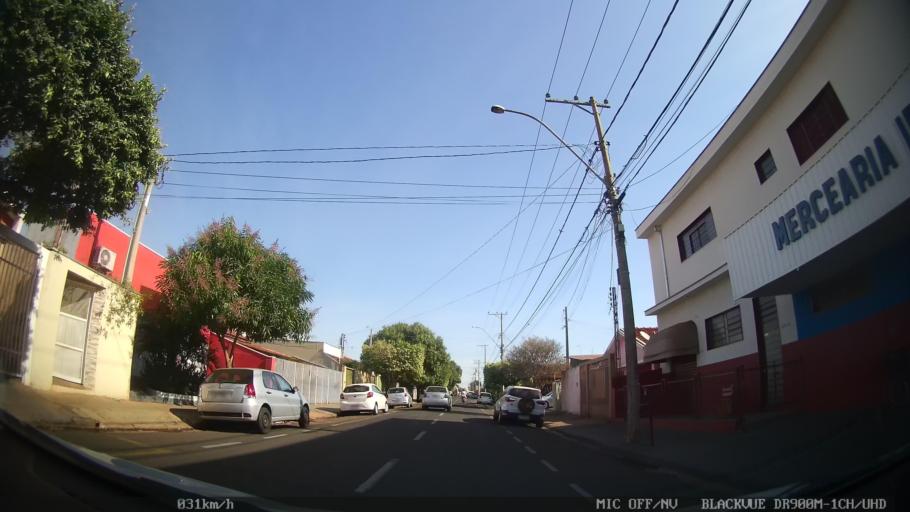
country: BR
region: Sao Paulo
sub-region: Sao Jose Do Rio Preto
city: Sao Jose do Rio Preto
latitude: -20.8072
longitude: -49.3968
